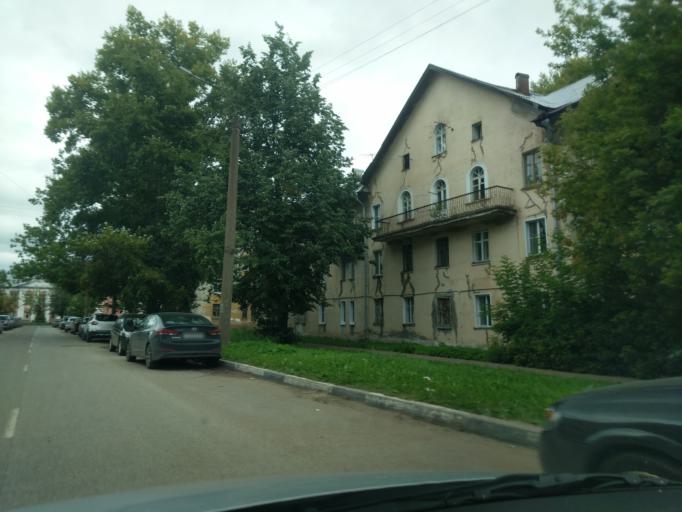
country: RU
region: Kirov
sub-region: Kirovo-Chepetskiy Rayon
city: Kirov
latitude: 58.6362
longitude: 49.6169
